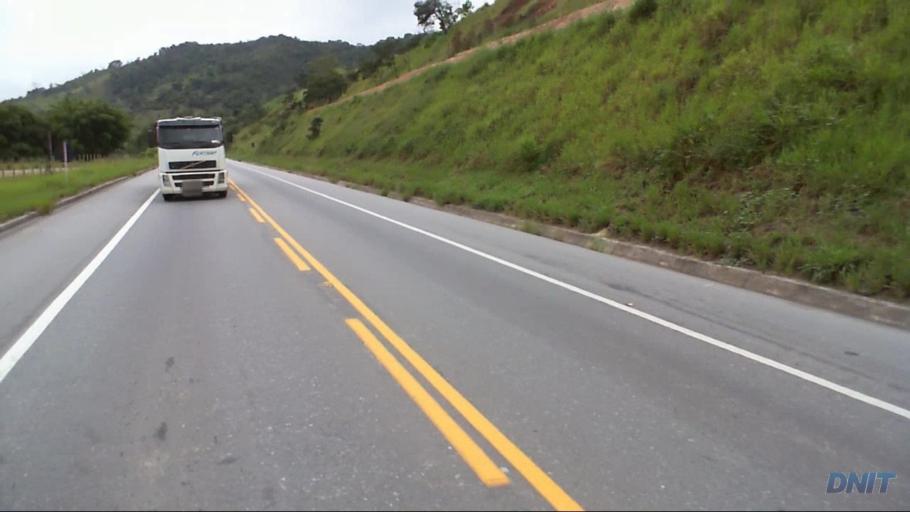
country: BR
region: Minas Gerais
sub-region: Nova Era
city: Nova Era
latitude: -19.7183
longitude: -43.0033
